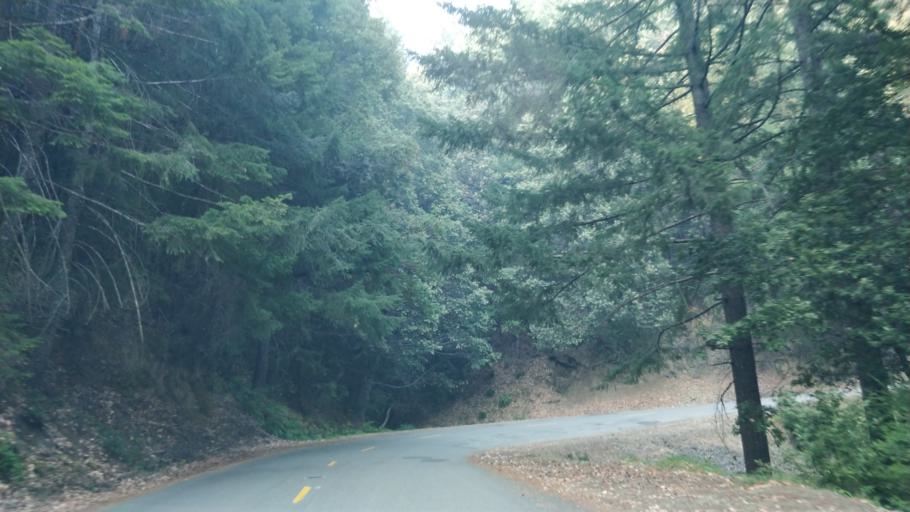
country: US
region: California
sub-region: Humboldt County
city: Rio Dell
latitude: 40.2788
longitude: -124.0699
